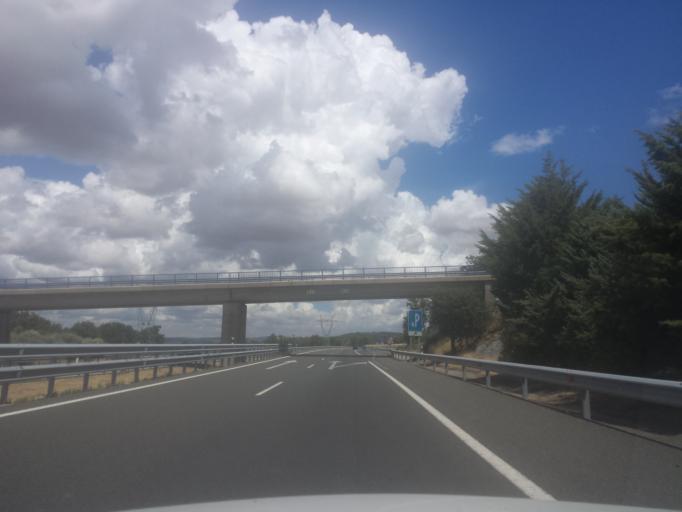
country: ES
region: Castille and Leon
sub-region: Provincia de Salamanca
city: Cantagallo
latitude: 40.3728
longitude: -5.8247
